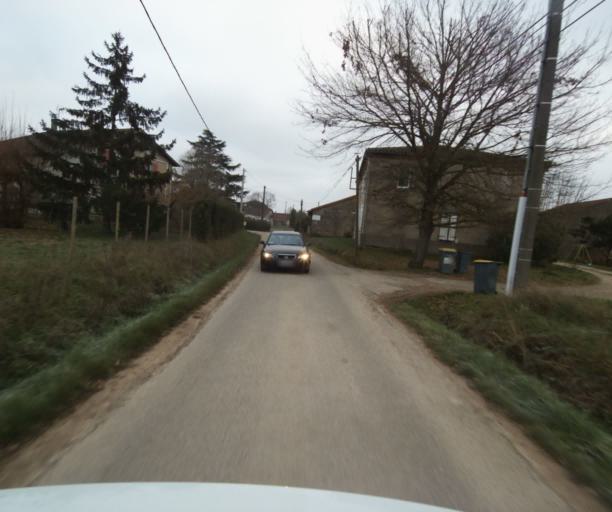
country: FR
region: Midi-Pyrenees
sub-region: Departement du Tarn-et-Garonne
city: Moissac
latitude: 44.1035
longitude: 1.1324
